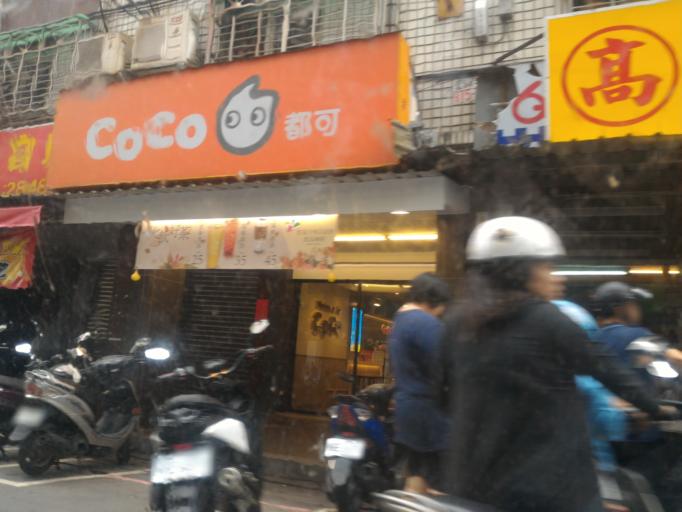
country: TW
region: Taipei
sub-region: Taipei
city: Banqiao
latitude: 25.0874
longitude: 121.4573
